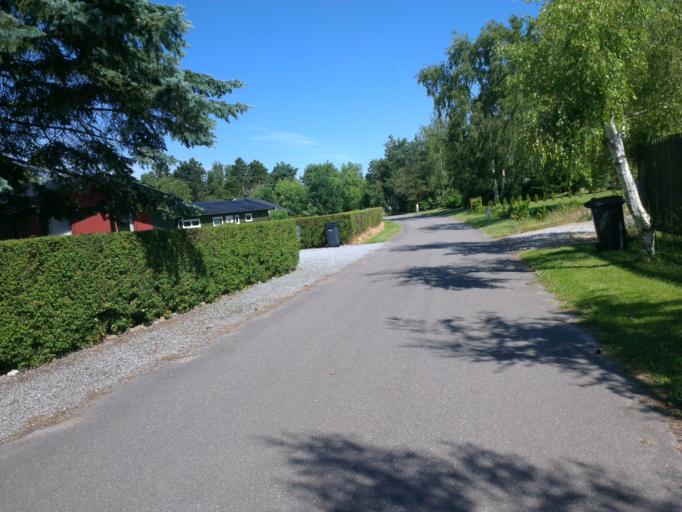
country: DK
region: Capital Region
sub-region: Frederikssund Kommune
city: Jaegerspris
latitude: 55.8163
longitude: 11.9441
